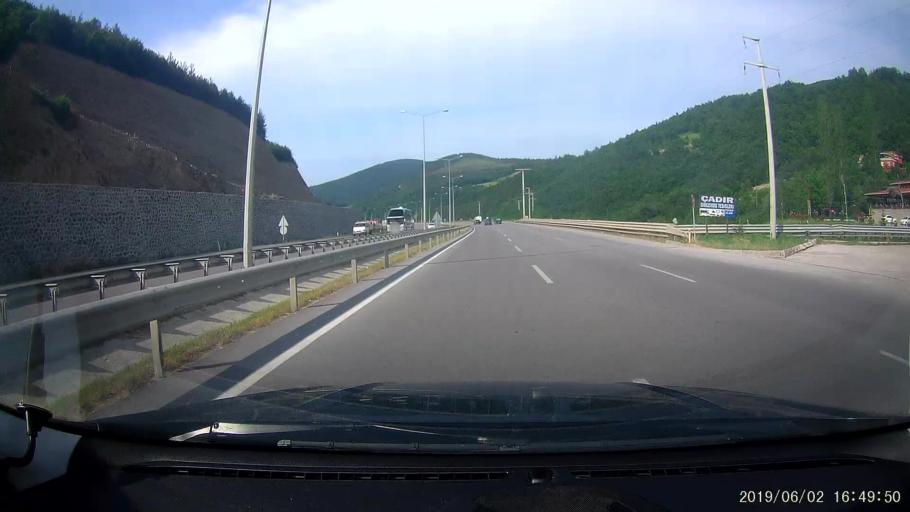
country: TR
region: Samsun
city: Samsun
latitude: 41.2429
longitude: 36.1696
